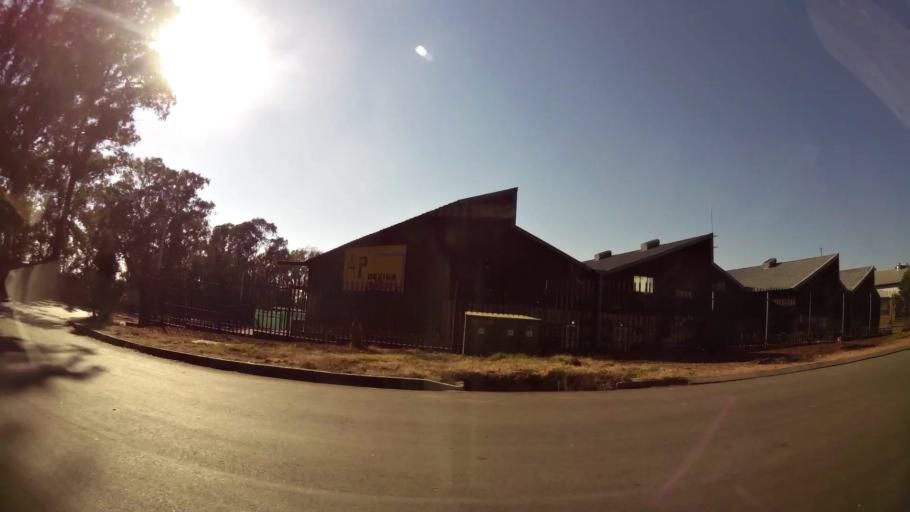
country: ZA
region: Gauteng
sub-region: City of Johannesburg Metropolitan Municipality
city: Modderfontein
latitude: -26.0653
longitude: 28.1870
